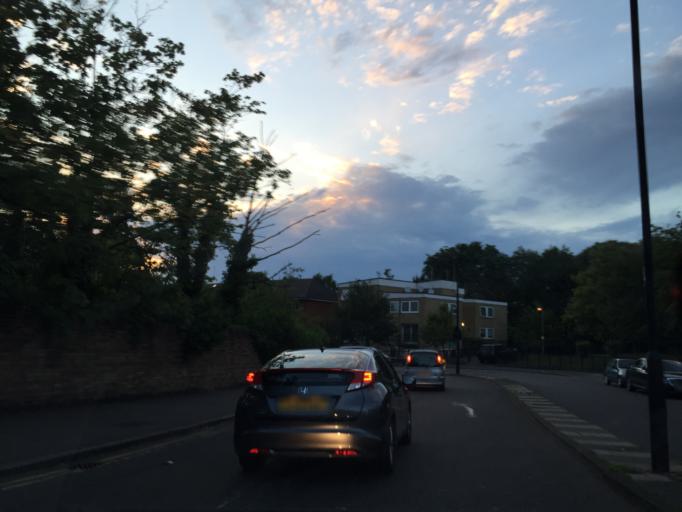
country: GB
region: England
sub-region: Greater London
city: Belsize Park
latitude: 51.5417
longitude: -0.1767
